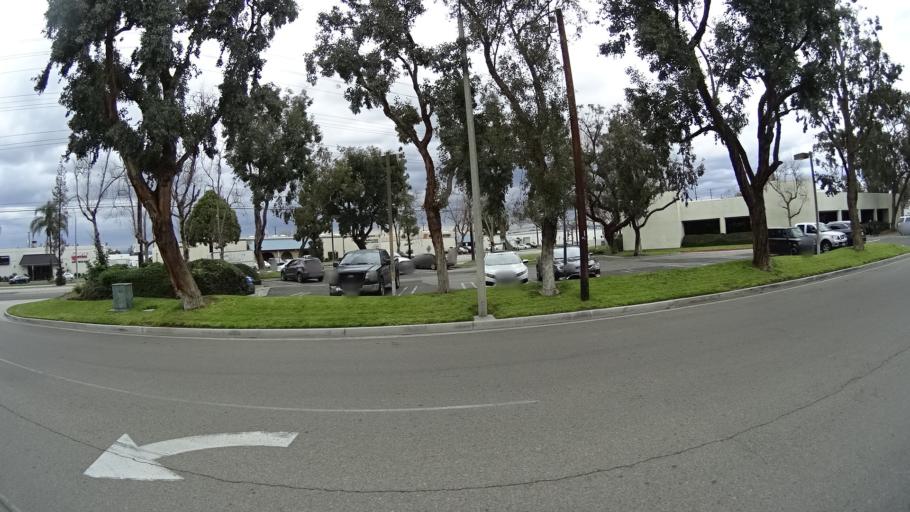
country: US
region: California
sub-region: Orange County
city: Placentia
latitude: 33.8487
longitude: -117.8648
